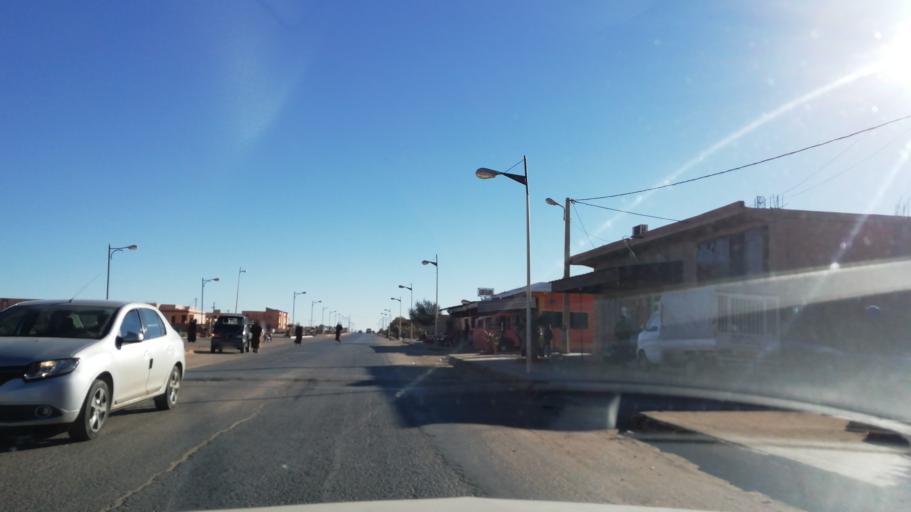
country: DZ
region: El Bayadh
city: El Bayadh
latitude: 33.8526
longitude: 0.6434
